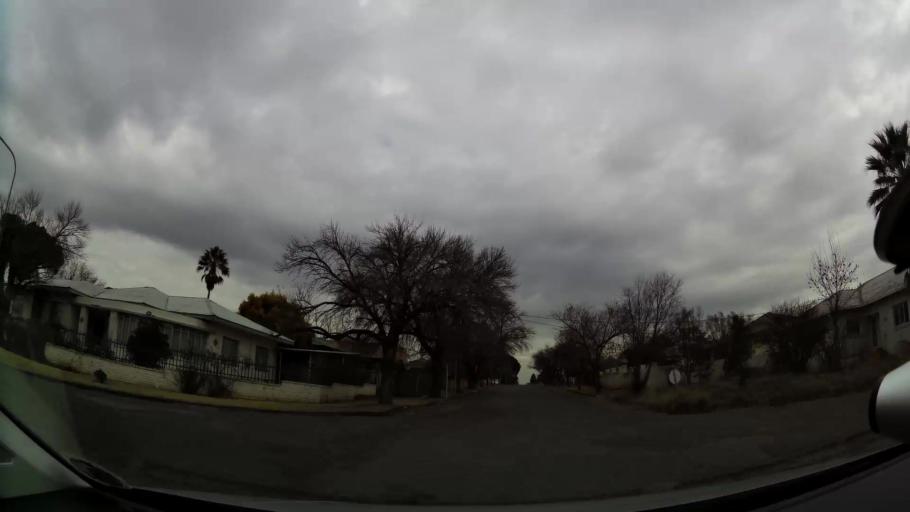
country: ZA
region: Orange Free State
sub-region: Fezile Dabi District Municipality
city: Kroonstad
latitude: -27.6535
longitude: 27.2447
